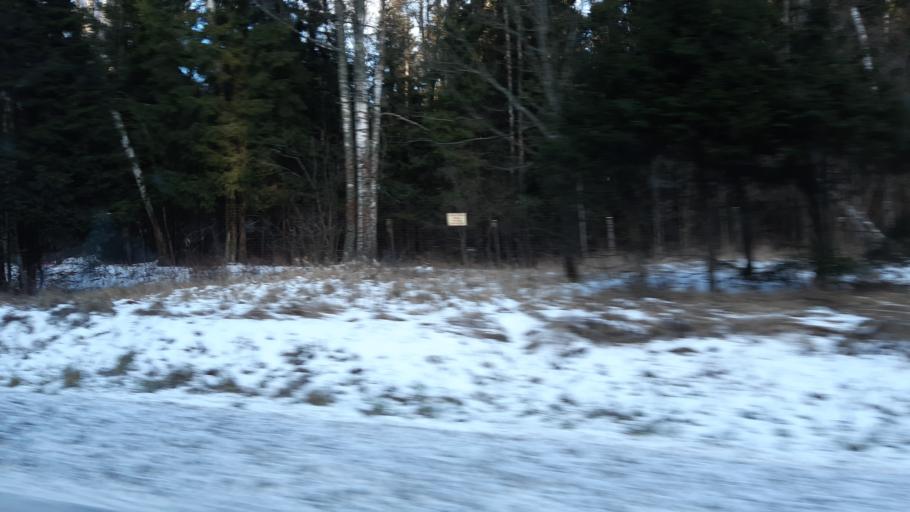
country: RU
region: Vladimir
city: Arsaki
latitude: 56.2695
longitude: 38.4216
